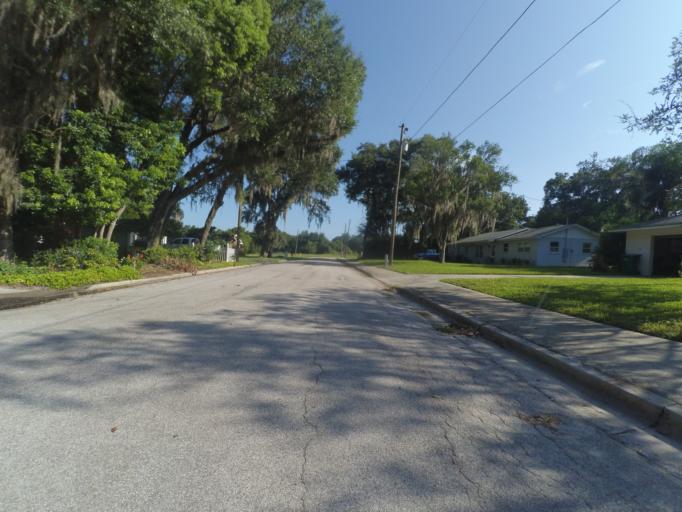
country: US
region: Florida
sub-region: Lake County
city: Umatilla
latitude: 28.9376
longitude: -81.6675
